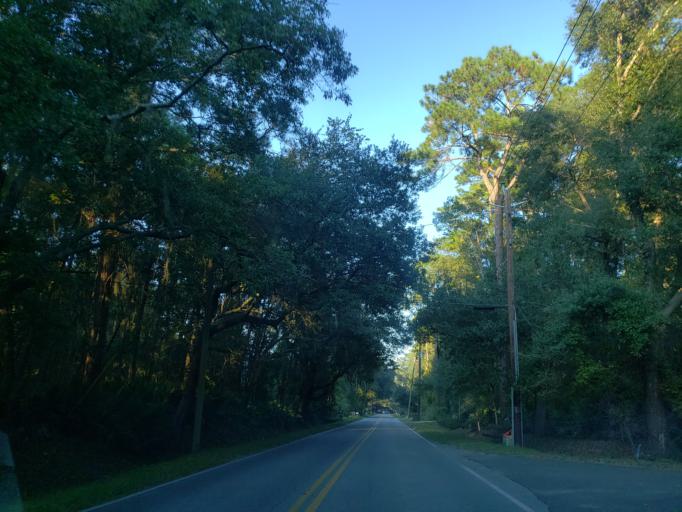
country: US
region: Georgia
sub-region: Chatham County
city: Isle of Hope
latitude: 31.9709
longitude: -81.0869
